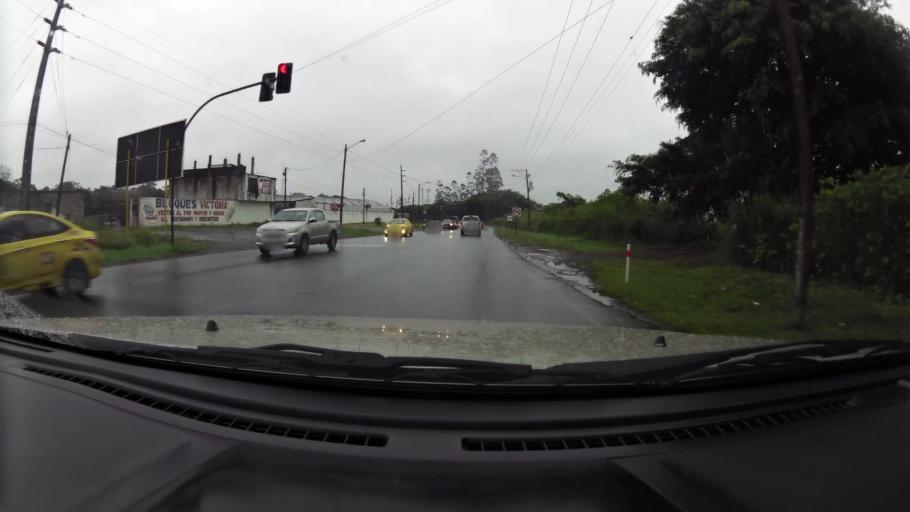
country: EC
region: Santo Domingo de los Tsachilas
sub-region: Canton Santo Domingo de los Colorados
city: Santo Domingo de los Colorados
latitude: -0.2402
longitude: -79.1515
